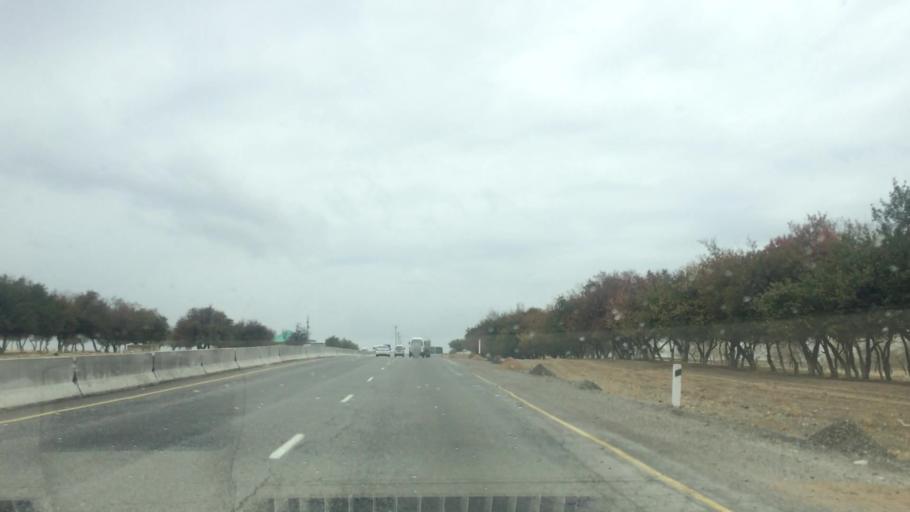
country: UZ
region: Samarqand
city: Bulung'ur
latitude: 39.8564
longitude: 67.4669
